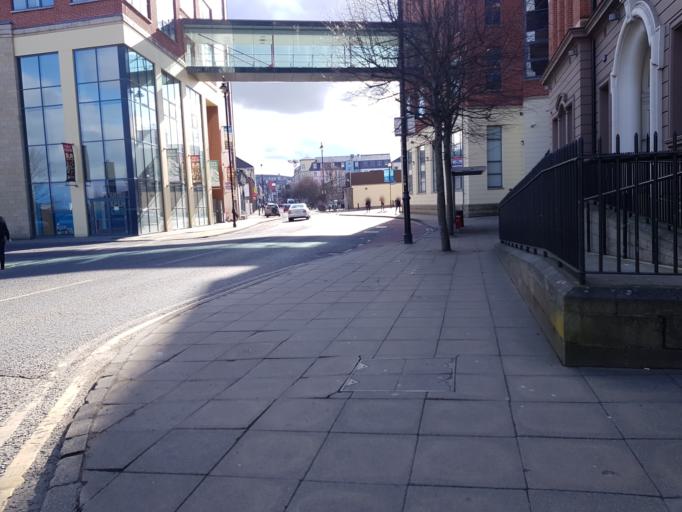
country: GB
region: Northern Ireland
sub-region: City of Derry
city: Derry
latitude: 55.0032
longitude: -7.3225
